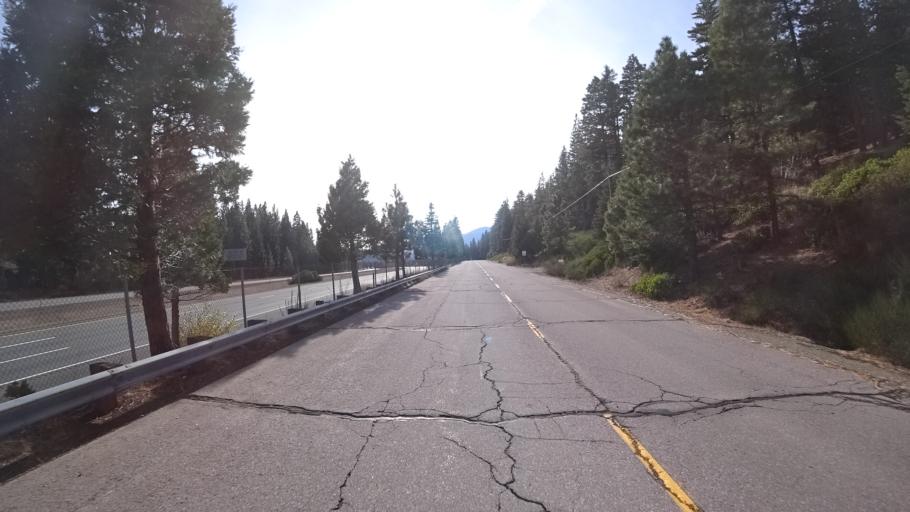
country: US
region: California
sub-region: Siskiyou County
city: Weed
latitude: 41.4064
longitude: -122.3815
